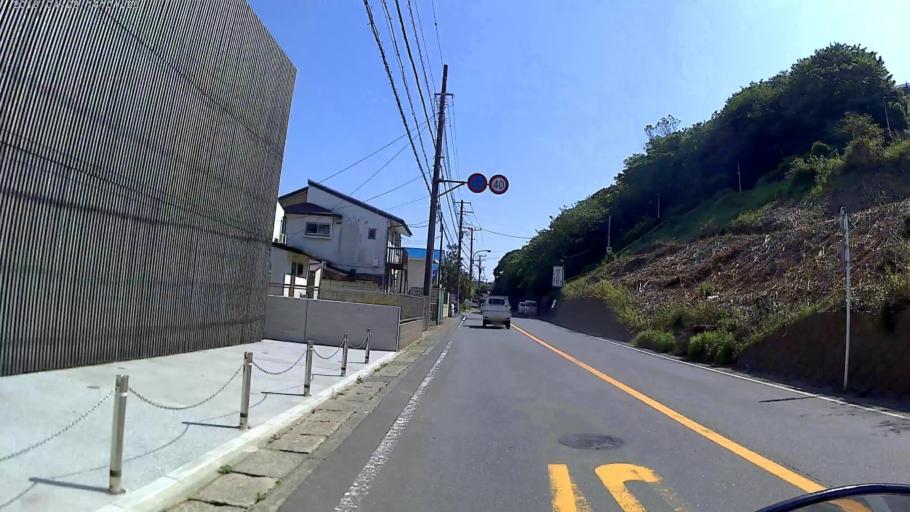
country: JP
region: Kanagawa
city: Miura
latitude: 35.1683
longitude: 139.6593
